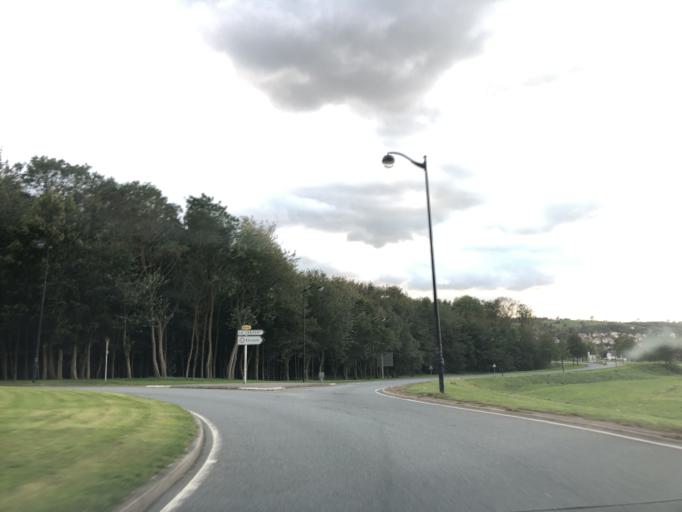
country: FR
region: Haute-Normandie
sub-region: Departement de la Seine-Maritime
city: Eu
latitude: 50.0532
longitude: 1.4032
